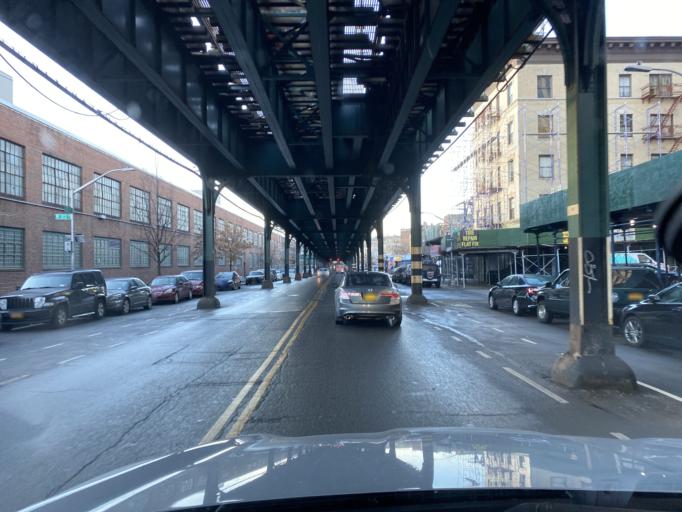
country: US
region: New York
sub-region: New York County
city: Inwood
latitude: 40.8686
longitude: -73.9159
